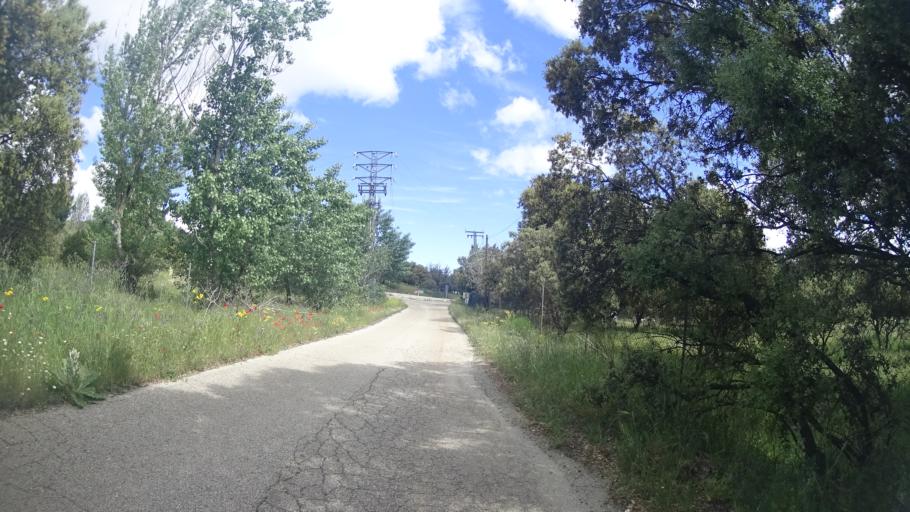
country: ES
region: Madrid
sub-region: Provincia de Madrid
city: Brunete
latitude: 40.4120
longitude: -3.9511
